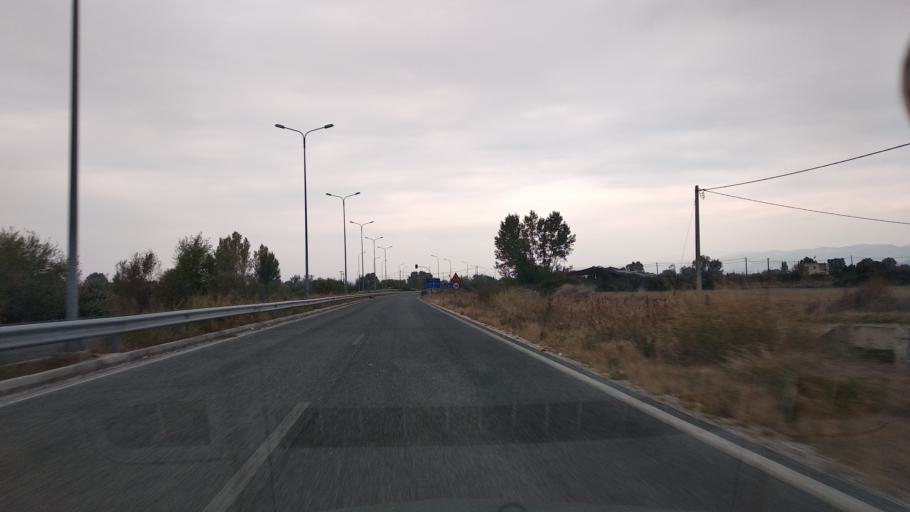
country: GR
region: Thessaly
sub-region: Trikala
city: Pyrgetos
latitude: 39.5550
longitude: 21.7340
